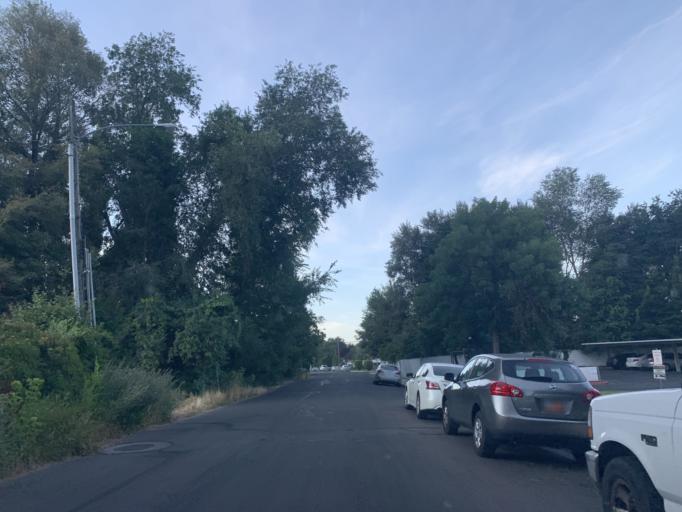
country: US
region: Utah
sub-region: Utah County
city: Provo
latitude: 40.2509
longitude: -111.6711
